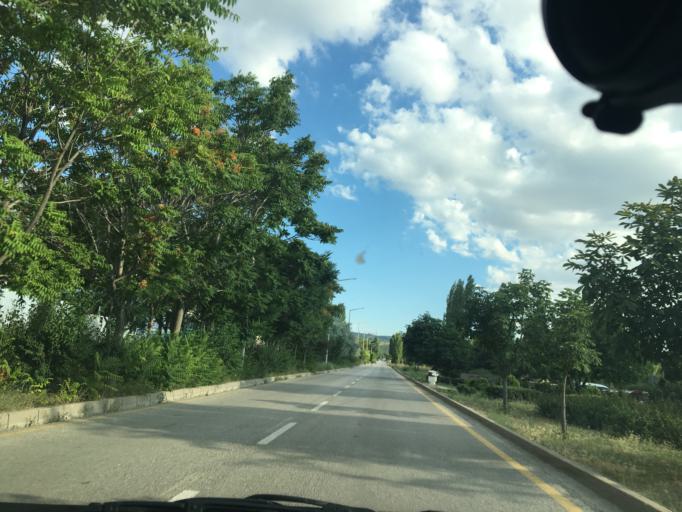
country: TR
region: Ankara
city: Ankara
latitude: 39.8971
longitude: 32.7769
